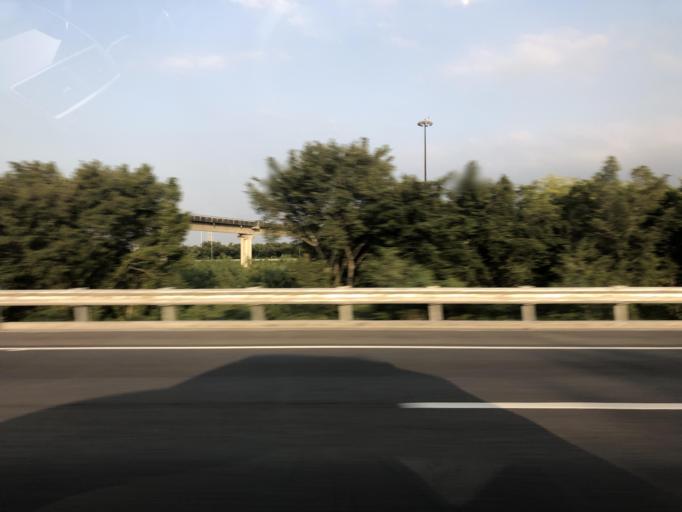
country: TW
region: Taiwan
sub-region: Tainan
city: Tainan
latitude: 23.0805
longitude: 120.2522
